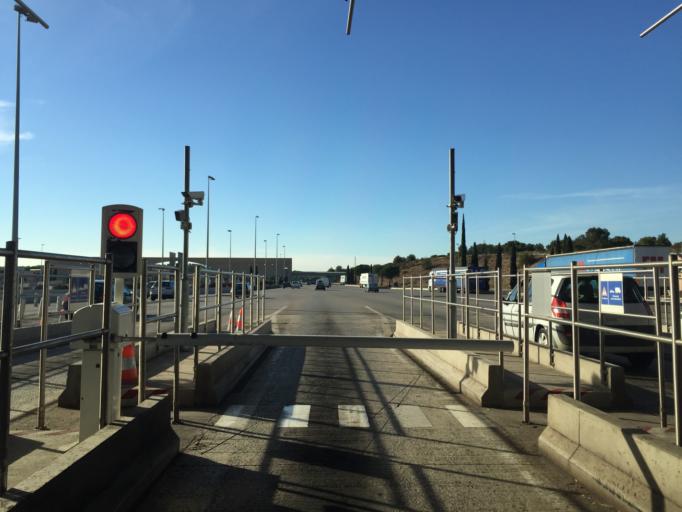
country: FR
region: Provence-Alpes-Cote d'Azur
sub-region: Departement des Bouches-du-Rhone
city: Lancon-Provence
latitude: 43.5934
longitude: 5.1769
